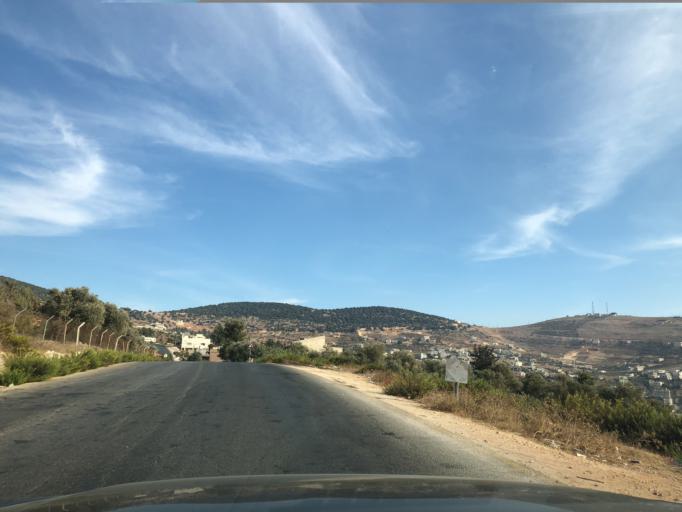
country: JO
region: Irbid
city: `Anjarah
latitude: 32.3185
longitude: 35.7654
